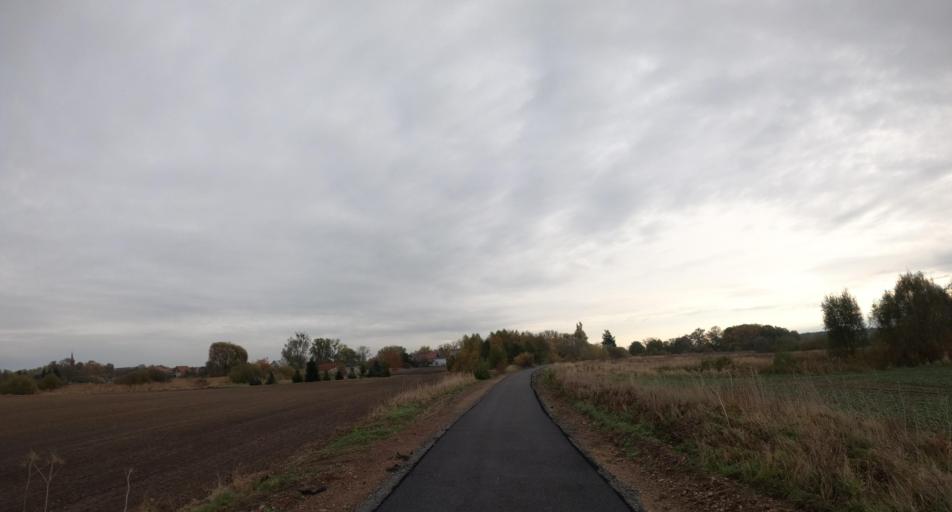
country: PL
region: West Pomeranian Voivodeship
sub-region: Powiat mysliborski
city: Nowogrodek Pomorski
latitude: 52.9868
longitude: 15.0570
